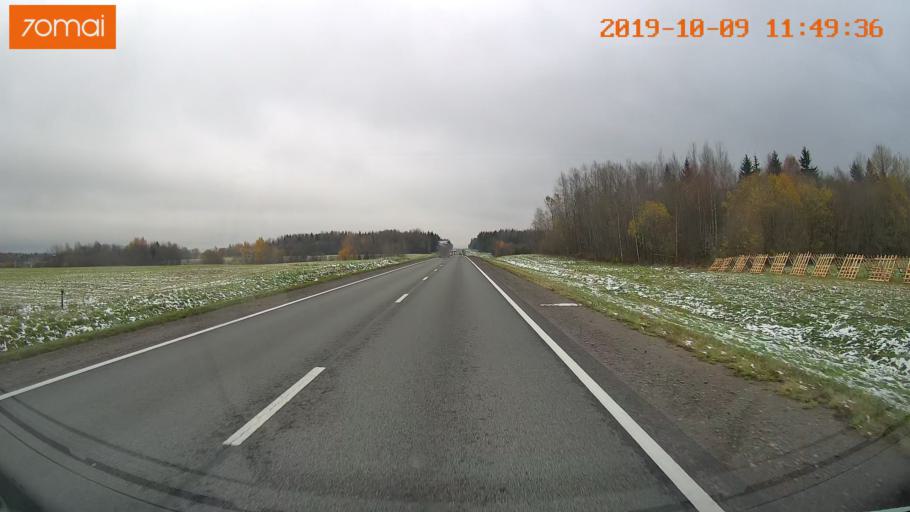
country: RU
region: Vologda
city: Gryazovets
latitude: 58.8164
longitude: 40.2327
